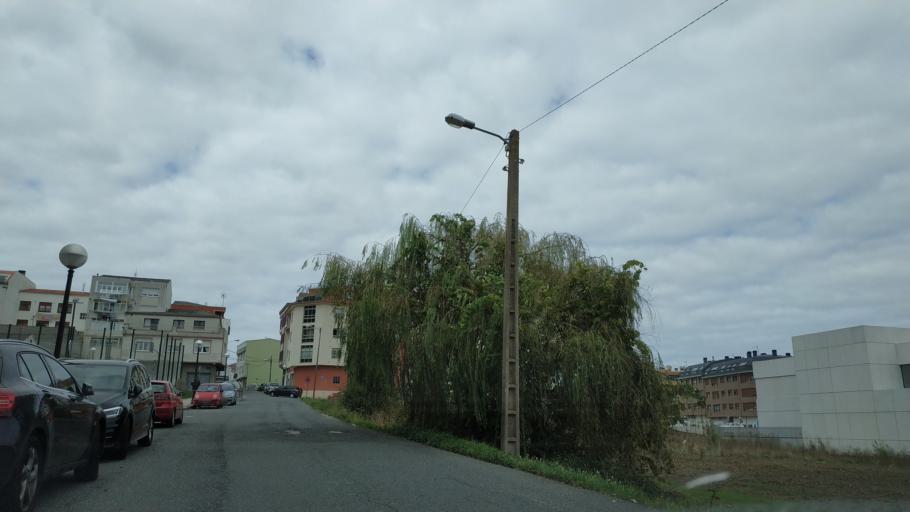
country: ES
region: Galicia
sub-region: Provincia da Coruna
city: Arteixo
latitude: 43.3008
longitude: -8.5085
